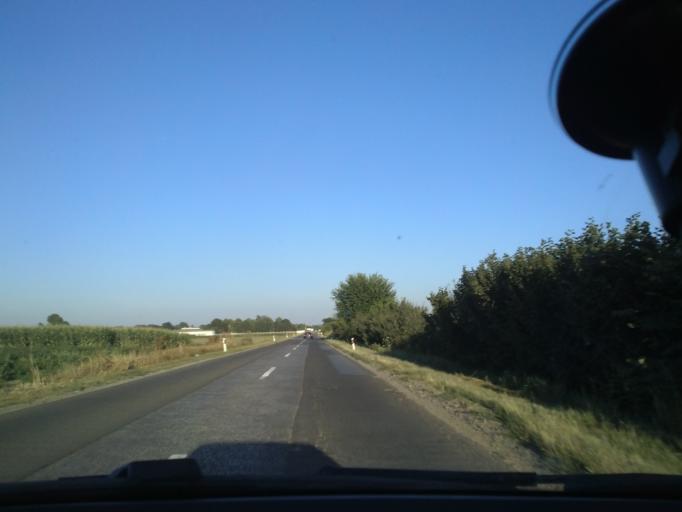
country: RS
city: Kisac
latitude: 45.3378
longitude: 19.6625
